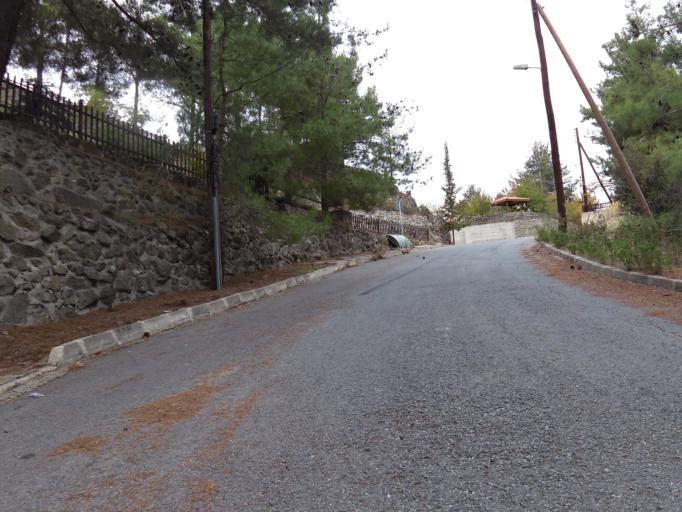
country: CY
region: Limassol
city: Kyperounta
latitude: 34.9265
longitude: 32.9401
